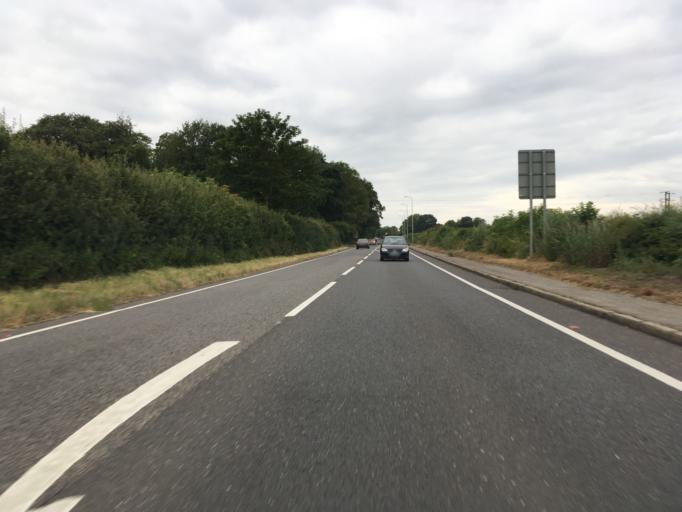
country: GB
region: England
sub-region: Central Bedfordshire
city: Kensworth
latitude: 51.8669
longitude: -0.4899
